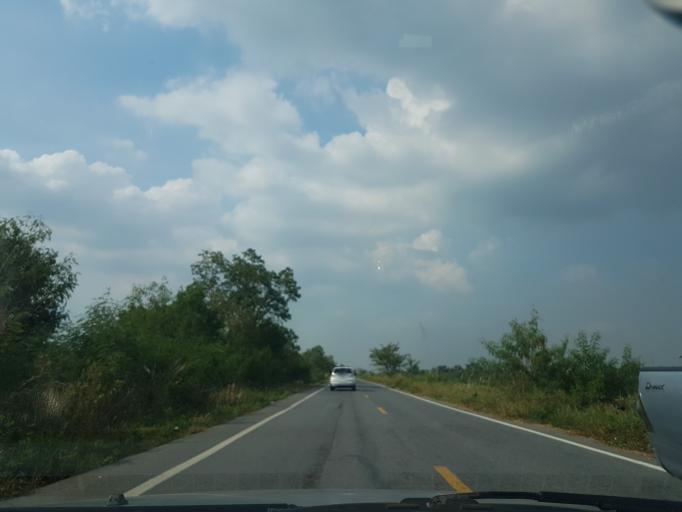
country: TH
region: Phra Nakhon Si Ayutthaya
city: Phachi
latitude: 14.4450
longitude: 100.7650
